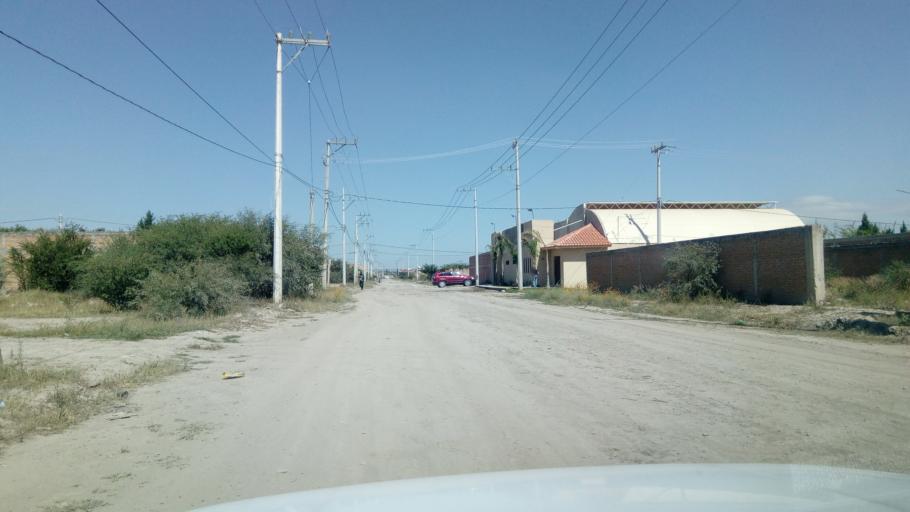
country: MX
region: Durango
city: Victoria de Durango
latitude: 23.9798
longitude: -104.6815
